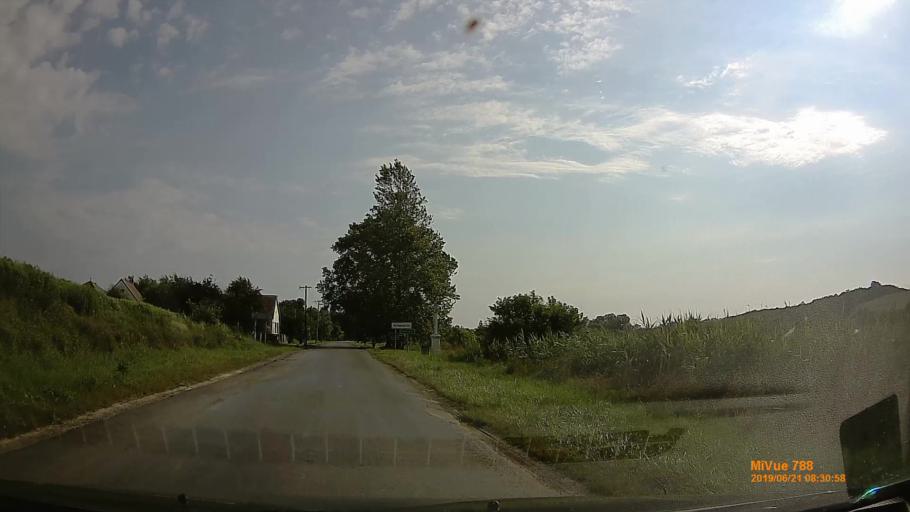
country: HU
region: Baranya
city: Szigetvar
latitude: 46.1502
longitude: 17.8646
